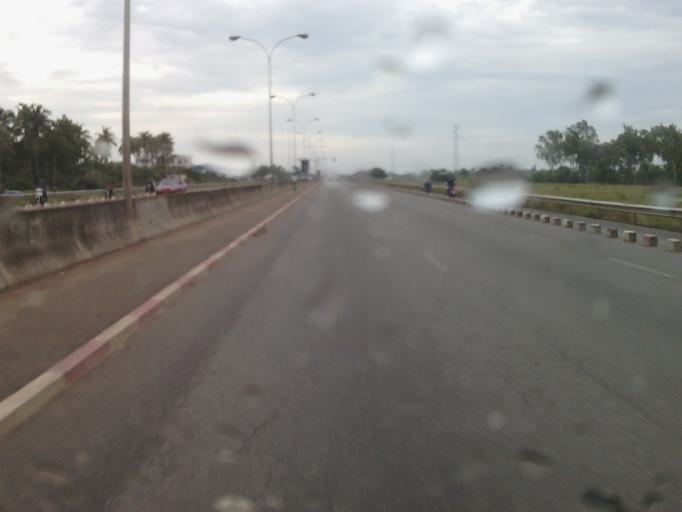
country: BJ
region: Queme
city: Porto-Novo
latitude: 6.3750
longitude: 2.5666
